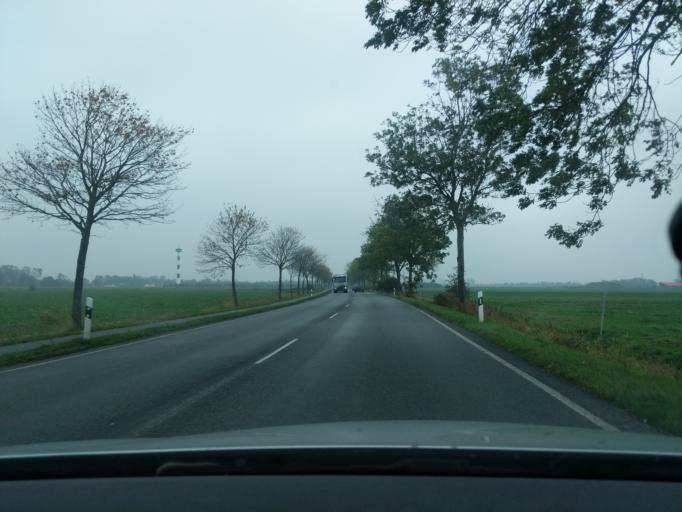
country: DE
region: Lower Saxony
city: Cuxhaven
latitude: 53.8310
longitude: 8.7454
